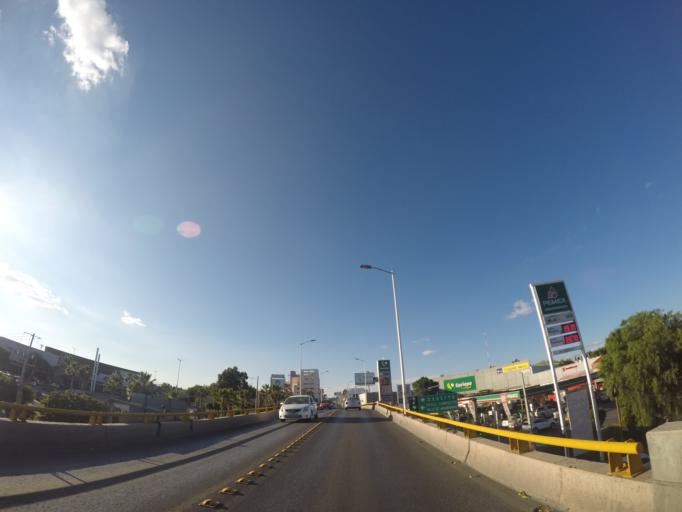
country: MX
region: San Luis Potosi
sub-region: San Luis Potosi
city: San Luis Potosi
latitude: 22.1601
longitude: -101.0003
